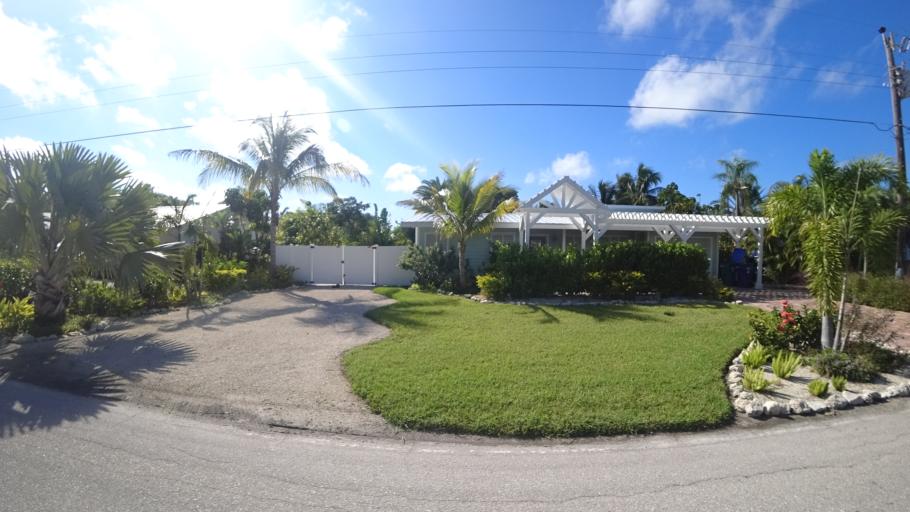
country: US
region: Florida
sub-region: Manatee County
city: Anna Maria
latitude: 27.5250
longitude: -82.7262
